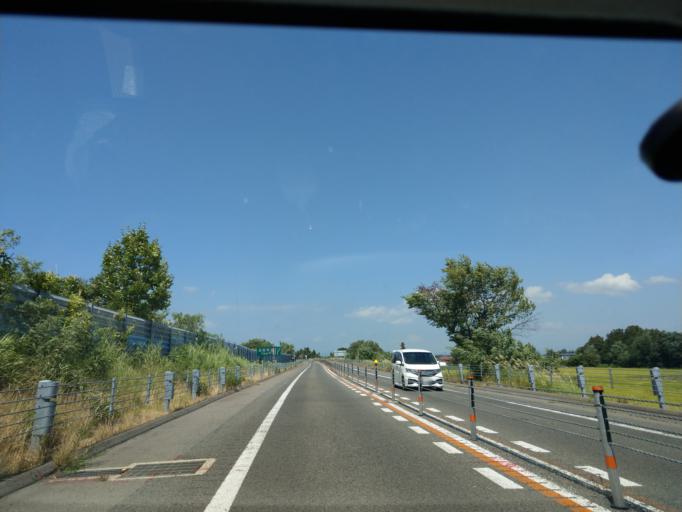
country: JP
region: Akita
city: Yokotemachi
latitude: 39.3398
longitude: 140.5013
